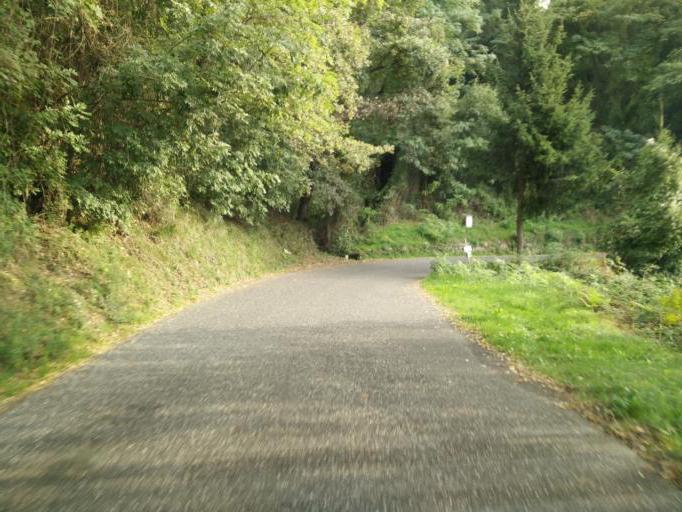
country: IT
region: Tuscany
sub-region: Provincia di Massa-Carrara
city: Pontremoli
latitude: 44.3731
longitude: 9.8490
